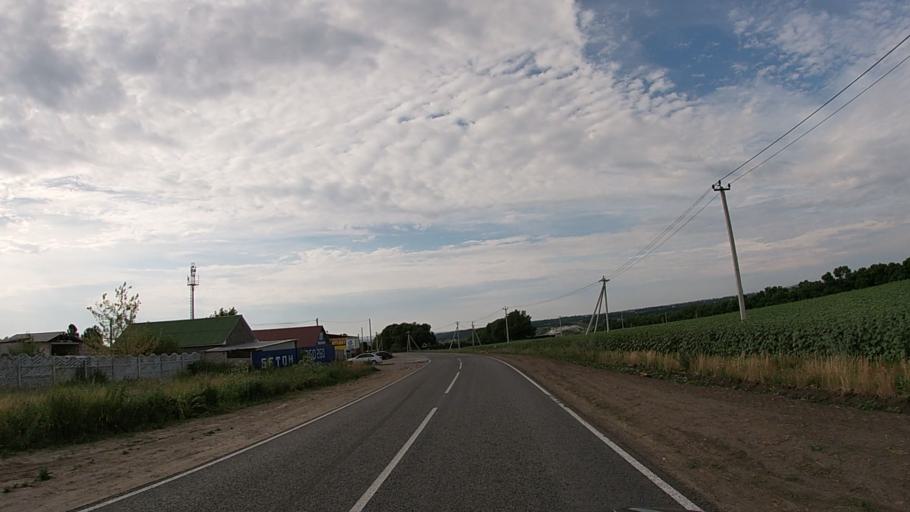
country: RU
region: Belgorod
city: Severnyy
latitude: 50.7207
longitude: 36.5849
